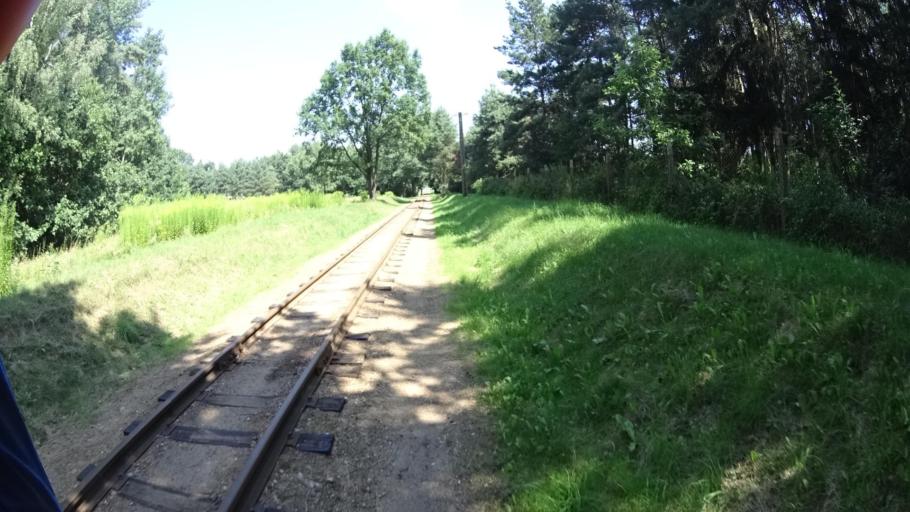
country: PL
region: Masovian Voivodeship
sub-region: Powiat piaseczynski
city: Tarczyn
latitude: 51.9958
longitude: 20.8973
